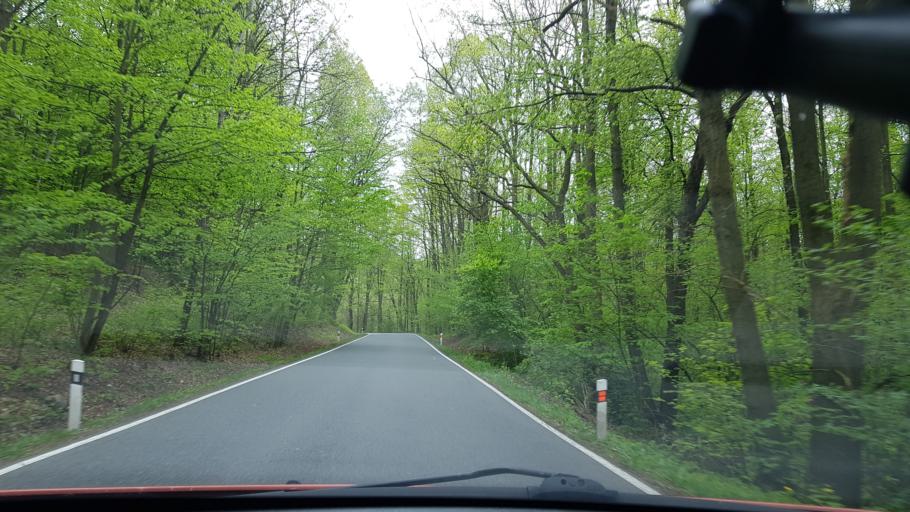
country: CZ
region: Olomoucky
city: Vidnava
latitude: 50.3679
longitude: 17.1934
